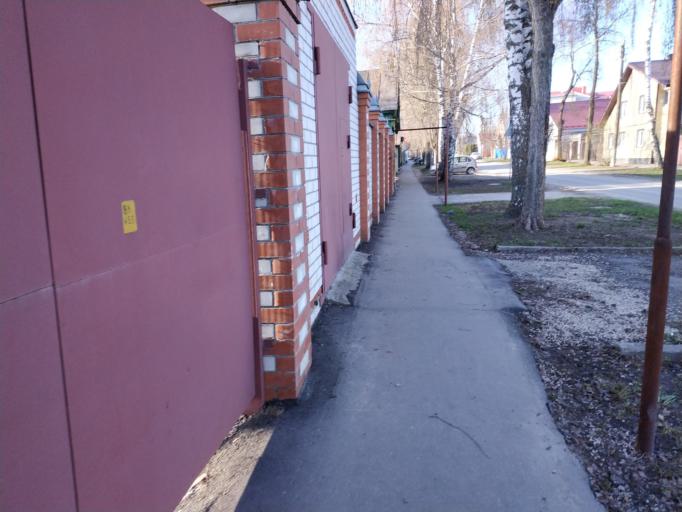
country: RU
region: Nizjnij Novgorod
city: Arzamas
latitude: 55.3964
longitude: 43.8146
